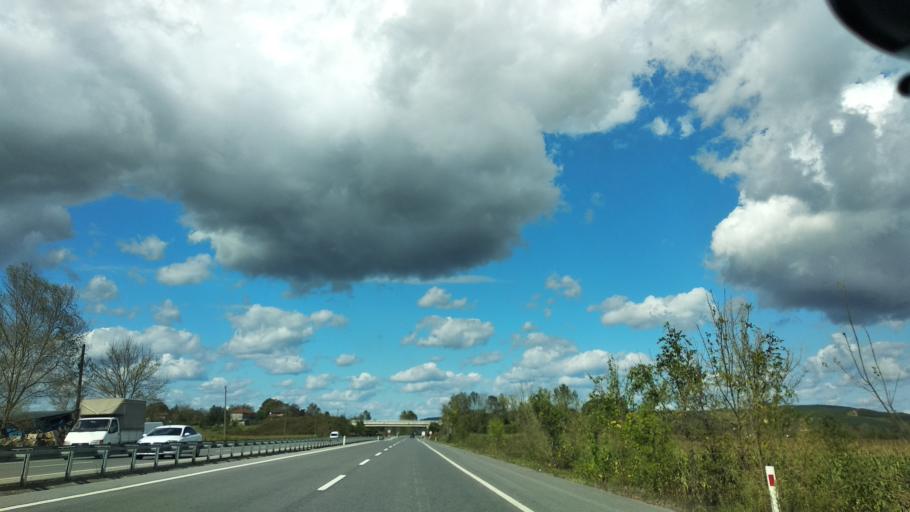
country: TR
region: Sakarya
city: Ortakoy
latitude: 41.0203
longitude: 30.6138
